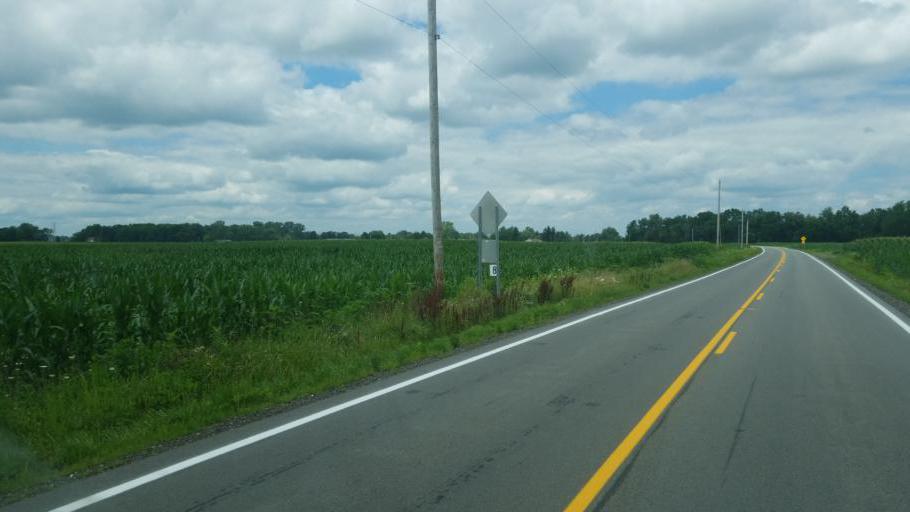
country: US
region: Ohio
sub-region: Richland County
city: Shelby
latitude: 40.8226
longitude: -82.6539
